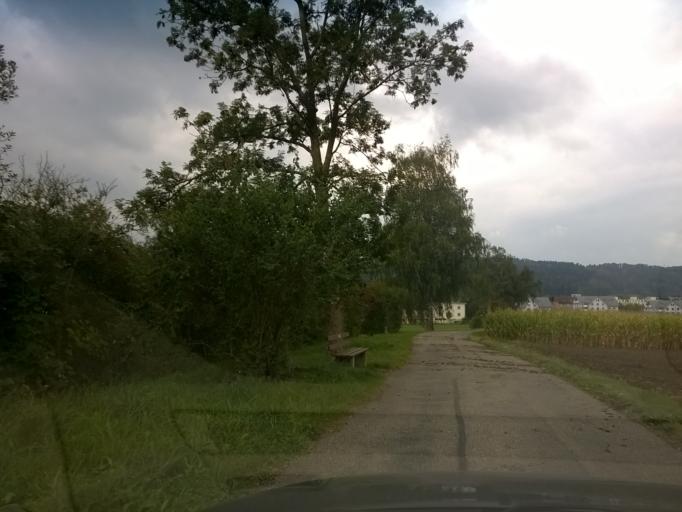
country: CH
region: Zurich
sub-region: Bezirk Buelach
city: Embrach
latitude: 47.5098
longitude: 8.6021
